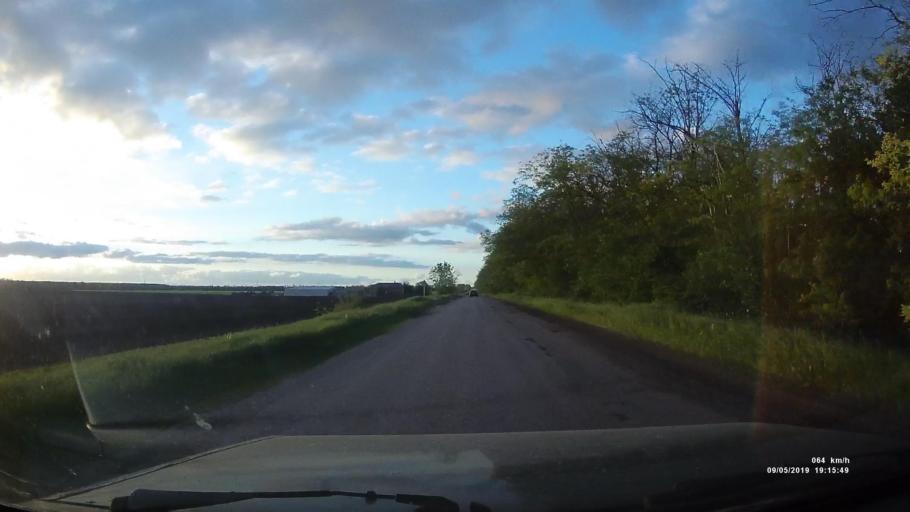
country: RU
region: Krasnodarskiy
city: Kanelovskaya
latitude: 46.7720
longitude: 39.2114
